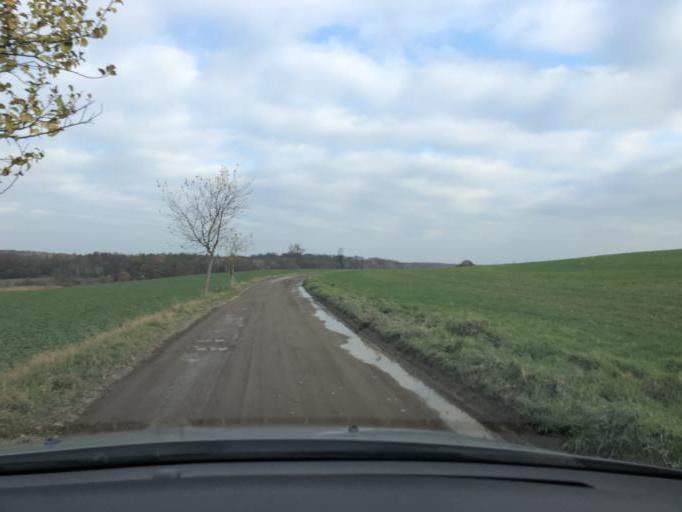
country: DE
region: Saxony
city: Mutzschen
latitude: 51.2784
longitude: 12.8896
